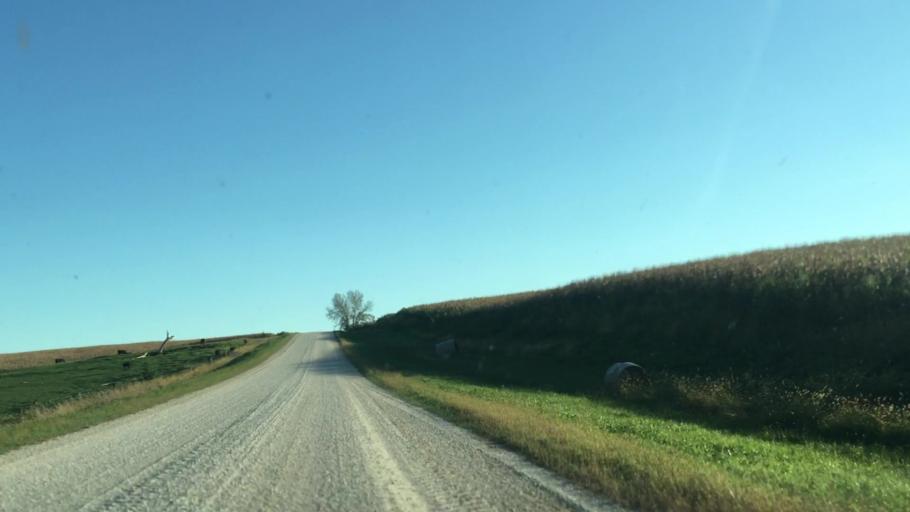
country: US
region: Minnesota
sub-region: Fillmore County
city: Preston
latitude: 43.8059
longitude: -92.0395
